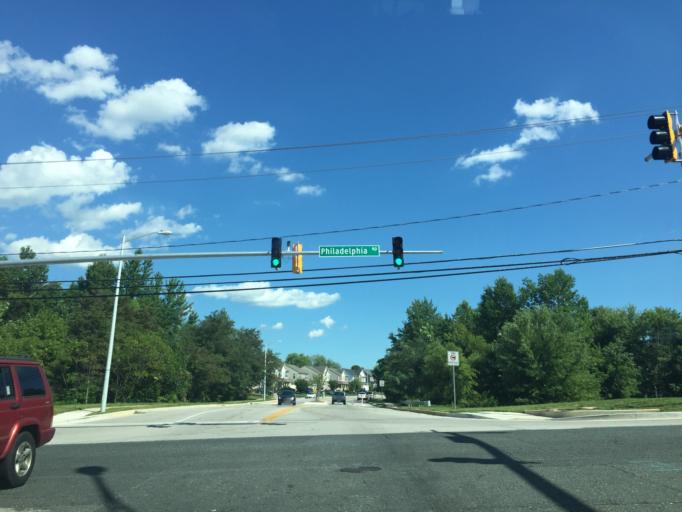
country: US
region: Maryland
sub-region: Baltimore County
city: White Marsh
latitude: 39.4073
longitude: -76.4128
